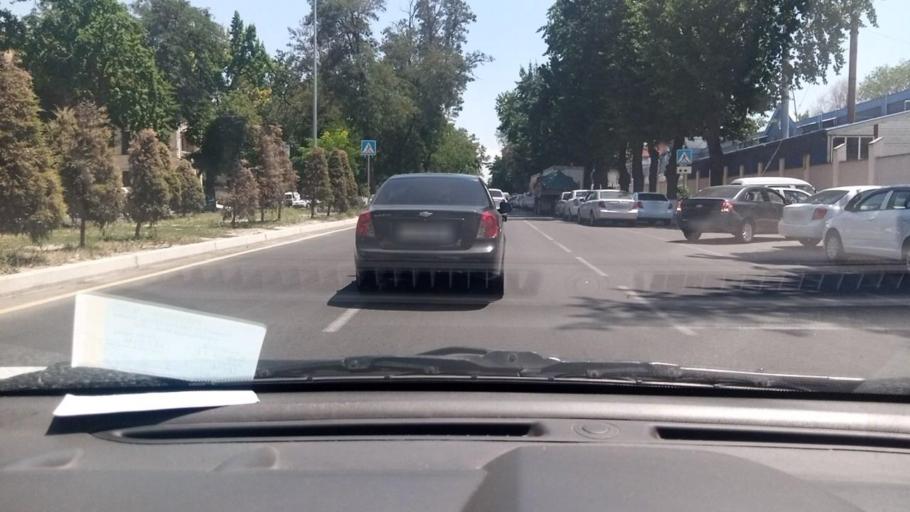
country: UZ
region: Toshkent Shahri
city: Tashkent
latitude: 41.2924
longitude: 69.1989
